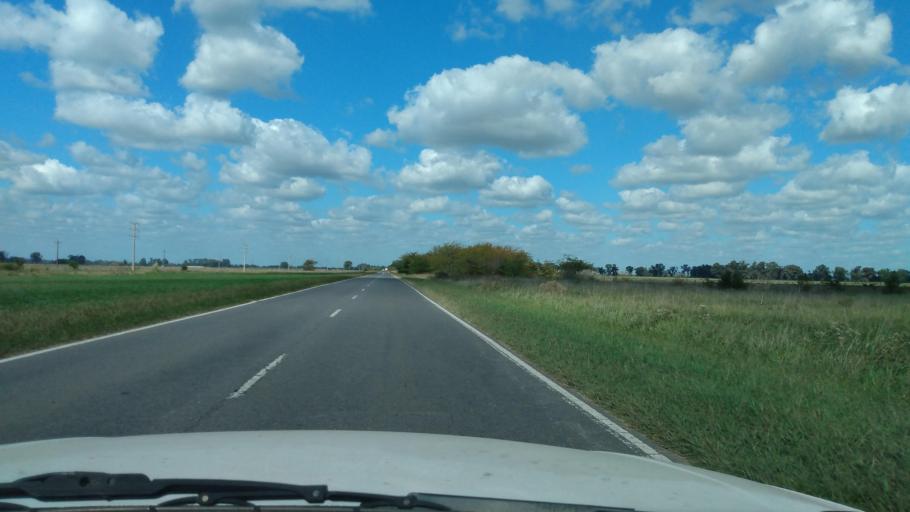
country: AR
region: Buenos Aires
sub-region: Partido de Navarro
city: Navarro
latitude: -34.9087
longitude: -59.3317
